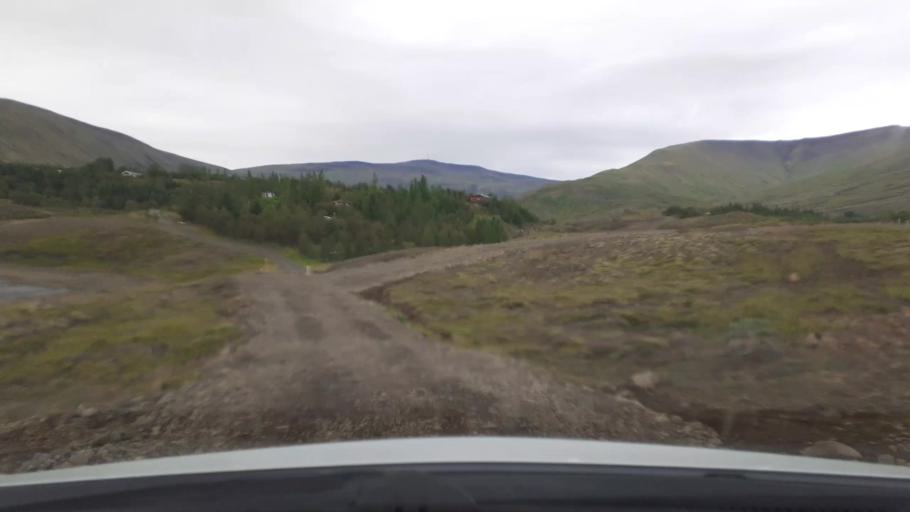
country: IS
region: Capital Region
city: Mosfellsbaer
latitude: 64.2889
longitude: -21.4611
